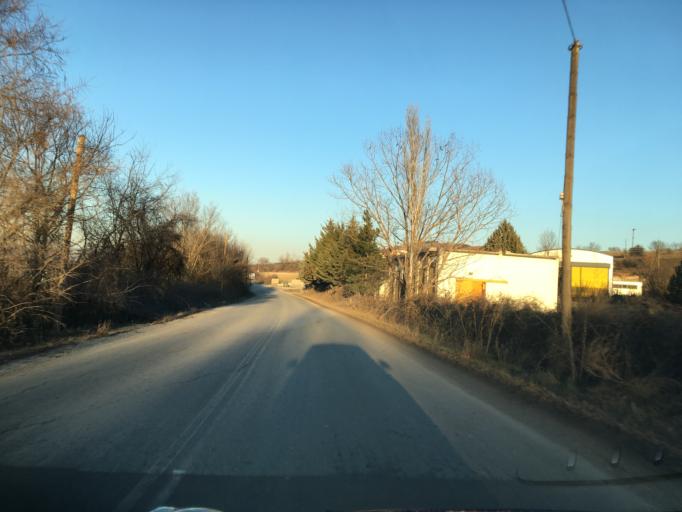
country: GR
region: West Macedonia
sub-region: Nomos Kozanis
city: Koila
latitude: 40.3245
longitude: 21.7835
